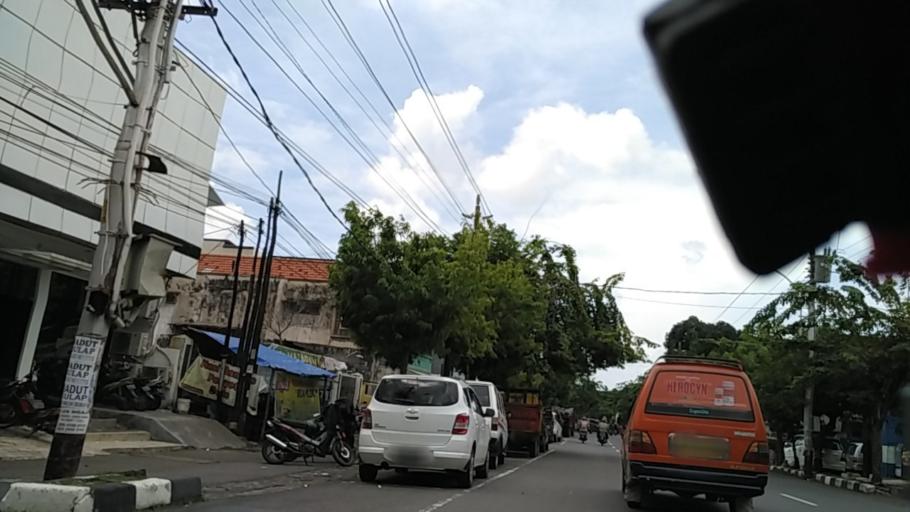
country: ID
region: Central Java
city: Semarang
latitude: -6.9918
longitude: 110.4320
